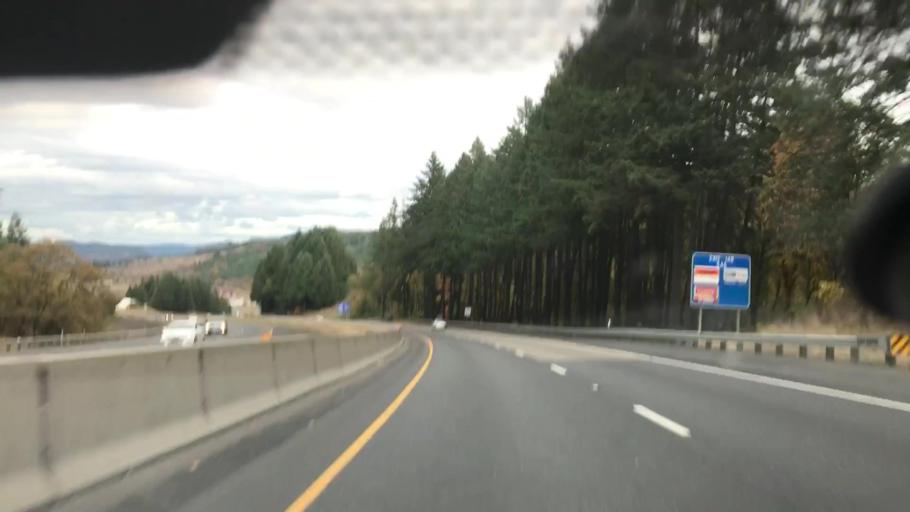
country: US
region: Oregon
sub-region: Douglas County
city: Yoncalla
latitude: 43.5279
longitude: -123.3030
